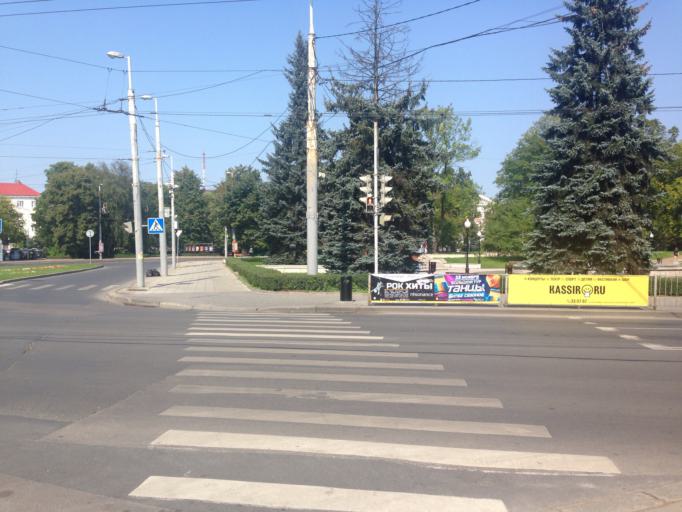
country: RU
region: Kaliningrad
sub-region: Gorod Kaliningrad
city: Kaliningrad
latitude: 54.7189
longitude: 20.4935
